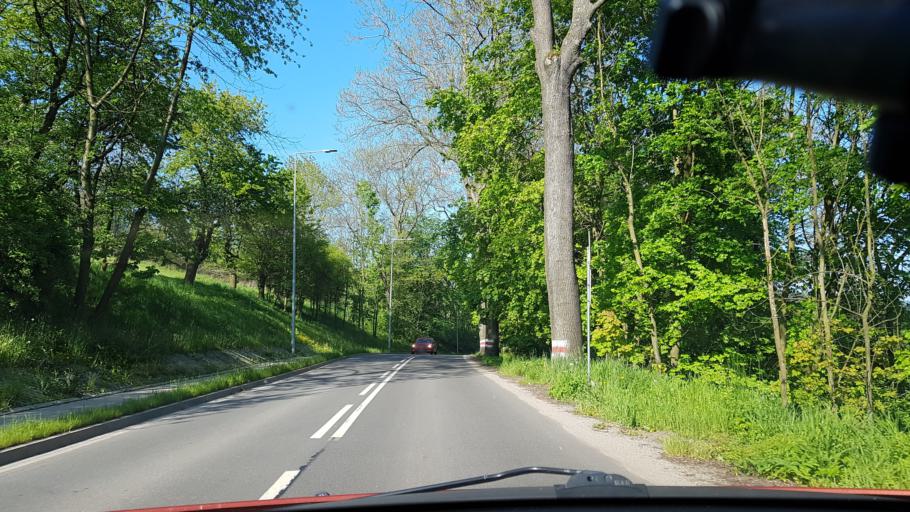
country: PL
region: Lower Silesian Voivodeship
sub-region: Powiat klodzki
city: Nowa Ruda
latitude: 50.5793
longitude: 16.4838
